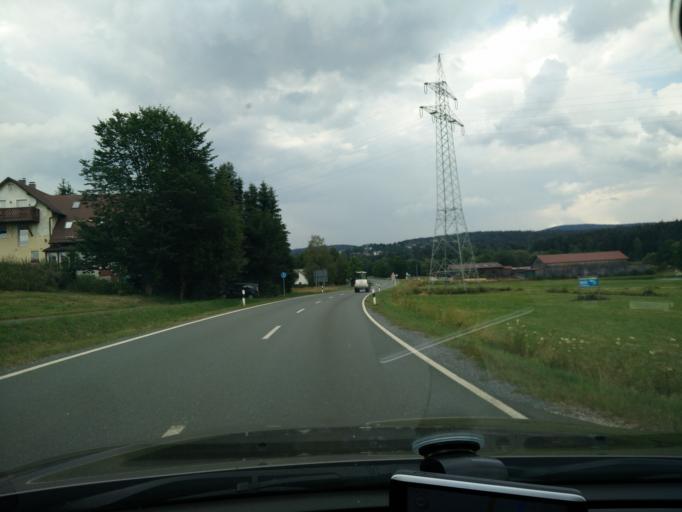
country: DE
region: Bavaria
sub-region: Upper Franconia
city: Fichtelberg
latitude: 49.9860
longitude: 11.8583
